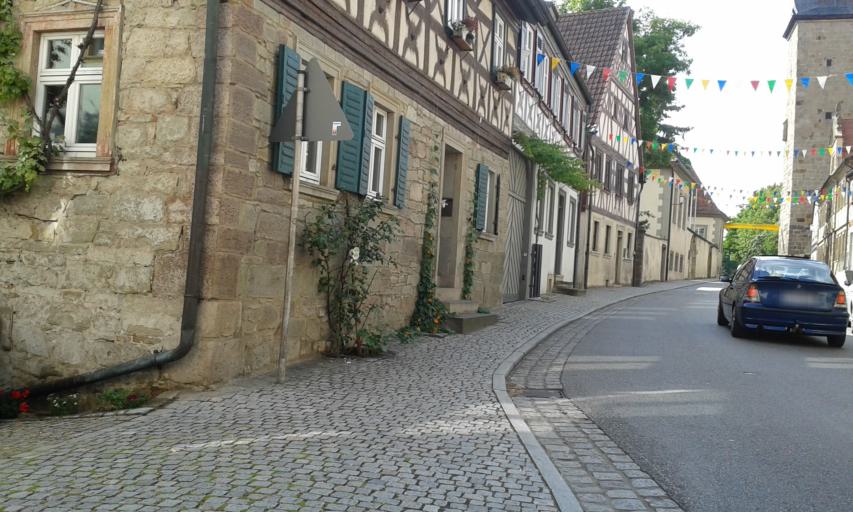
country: DE
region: Bavaria
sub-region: Regierungsbezirk Unterfranken
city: Zeil
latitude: 50.0099
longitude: 10.5939
